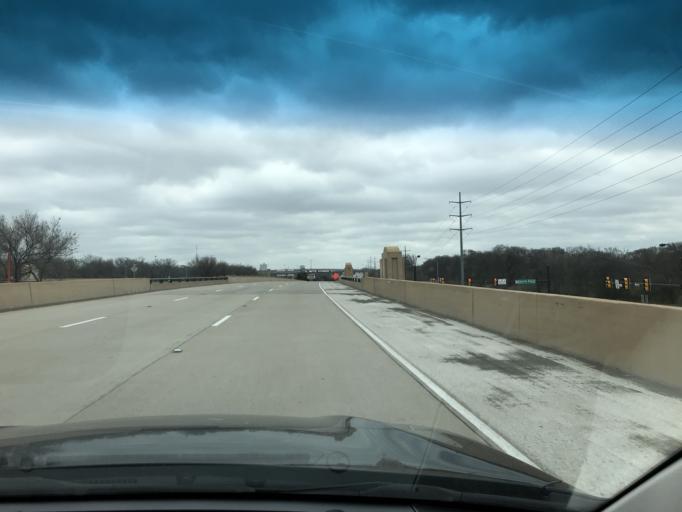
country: US
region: Texas
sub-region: Tarrant County
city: Westworth
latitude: 32.7123
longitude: -97.3992
